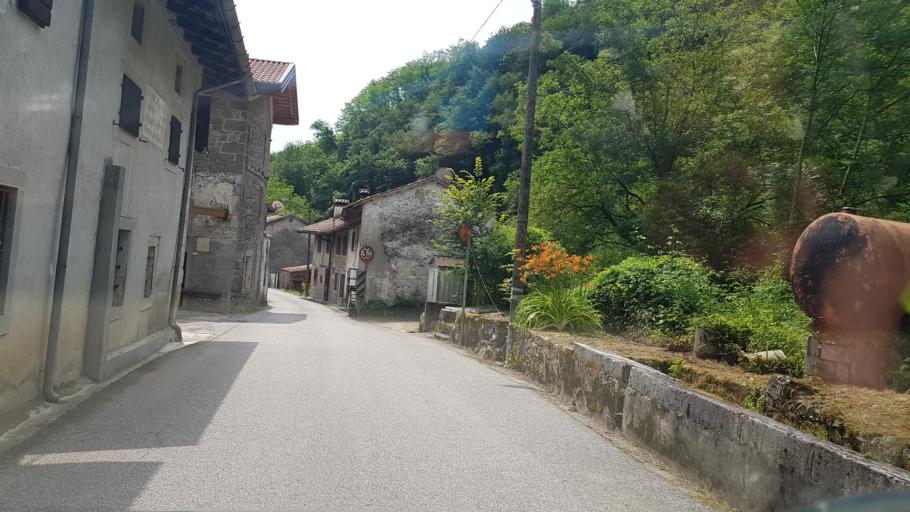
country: IT
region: Friuli Venezia Giulia
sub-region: Provincia di Udine
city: Torreano
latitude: 46.1524
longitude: 13.4344
